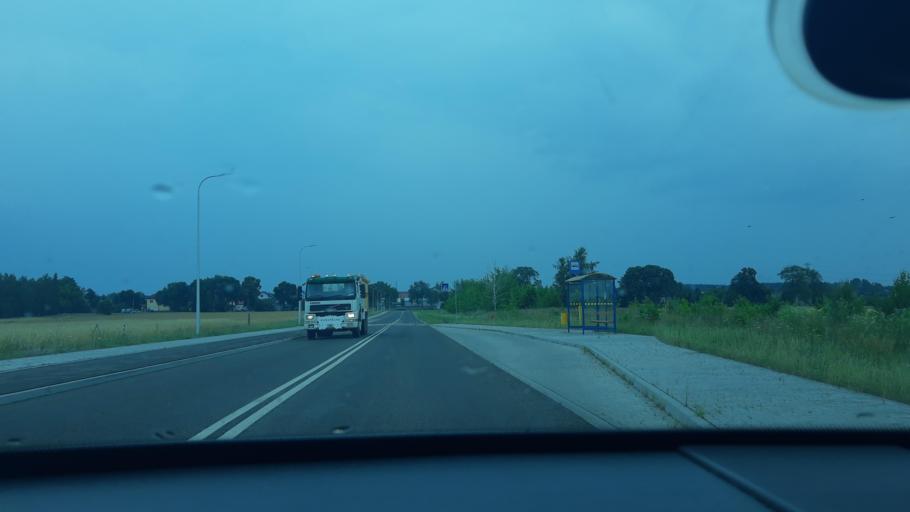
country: PL
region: Lodz Voivodeship
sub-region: Powiat sieradzki
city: Sieradz
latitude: 51.5732
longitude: 18.7004
